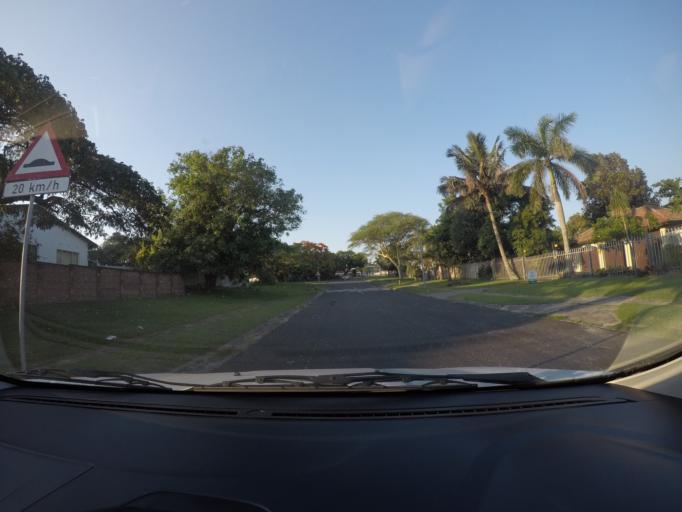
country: ZA
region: KwaZulu-Natal
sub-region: uThungulu District Municipality
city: Richards Bay
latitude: -28.7814
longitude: 32.0972
